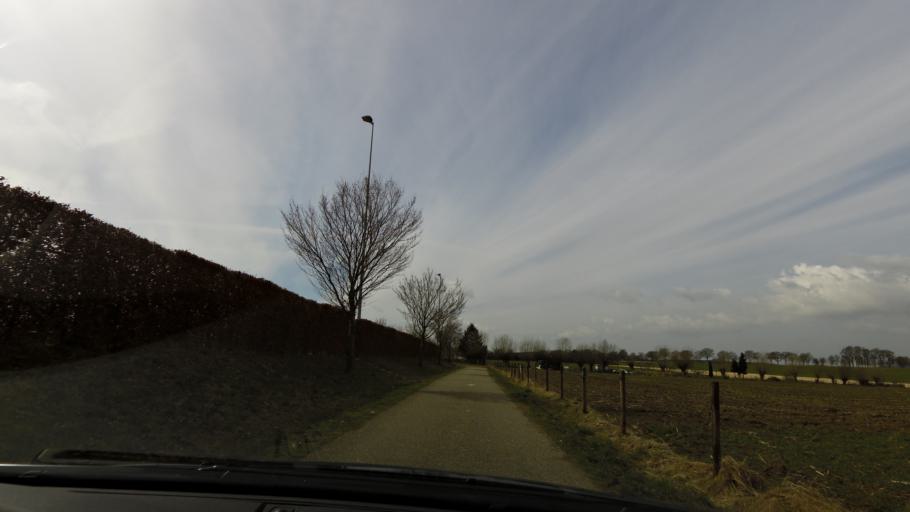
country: NL
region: Limburg
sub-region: Gemeente Simpelveld
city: Simpelveld
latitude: 50.8208
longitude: 5.9904
